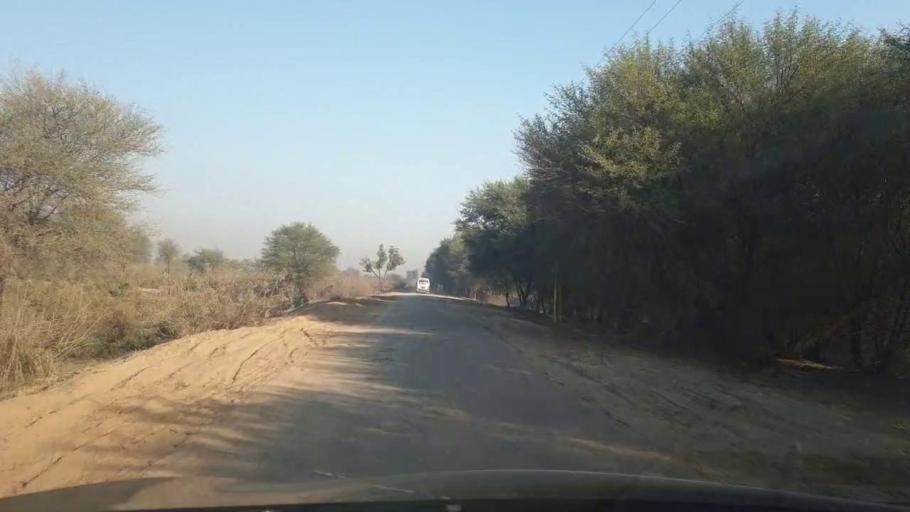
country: PK
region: Sindh
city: Mirpur Mathelo
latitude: 28.0646
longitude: 69.4650
